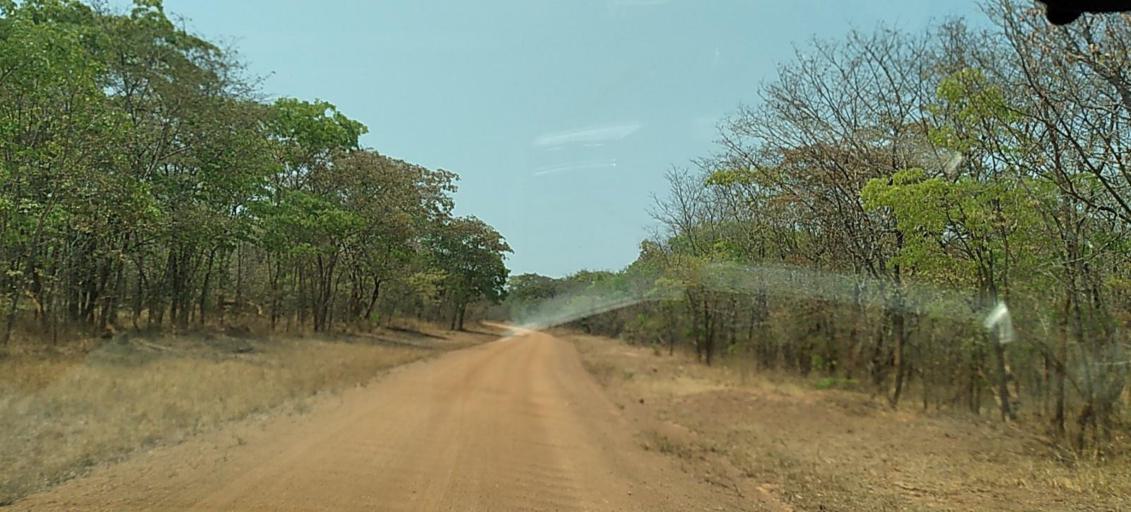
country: ZM
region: Central
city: Mumbwa
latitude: -14.2628
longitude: 26.5119
